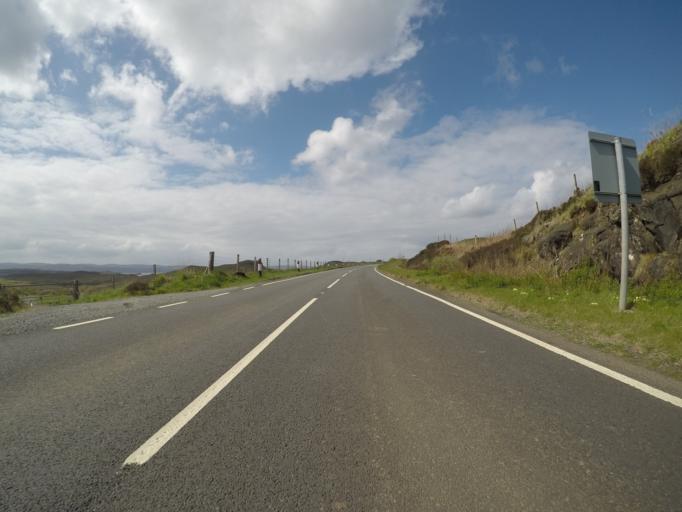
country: GB
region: Scotland
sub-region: Highland
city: Portree
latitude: 57.5325
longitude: -6.3548
